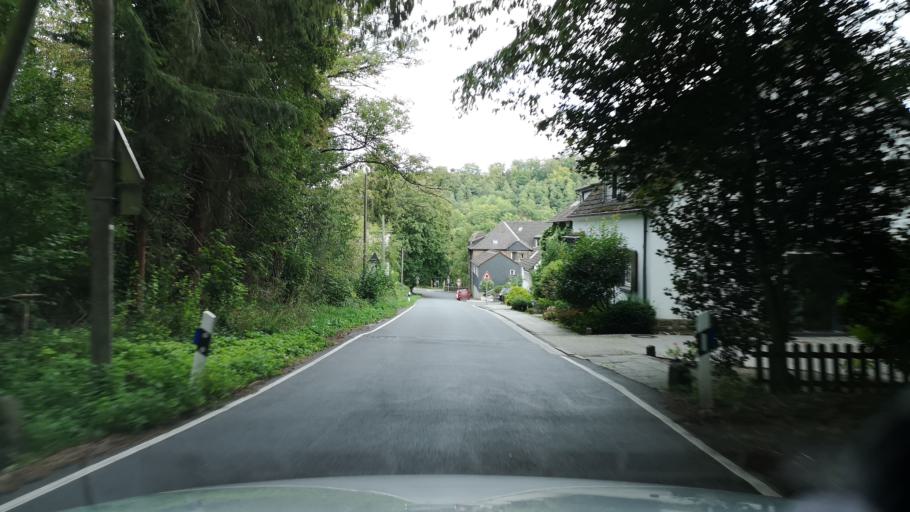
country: DE
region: North Rhine-Westphalia
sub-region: Regierungsbezirk Dusseldorf
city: Velbert
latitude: 51.3856
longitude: 7.1039
